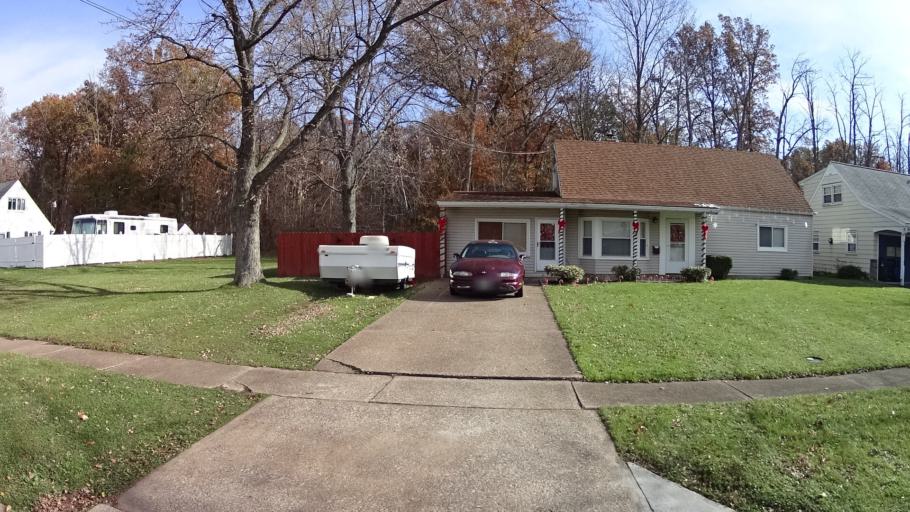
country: US
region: Ohio
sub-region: Lorain County
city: Sheffield Lake
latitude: 41.4845
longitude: -82.0872
